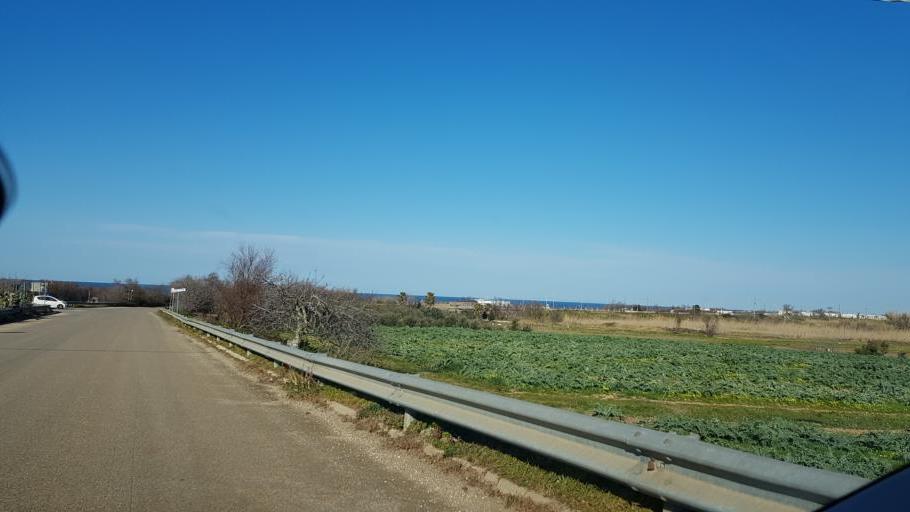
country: IT
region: Apulia
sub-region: Provincia di Brindisi
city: San Vito dei Normanni
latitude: 40.6919
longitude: 17.8266
